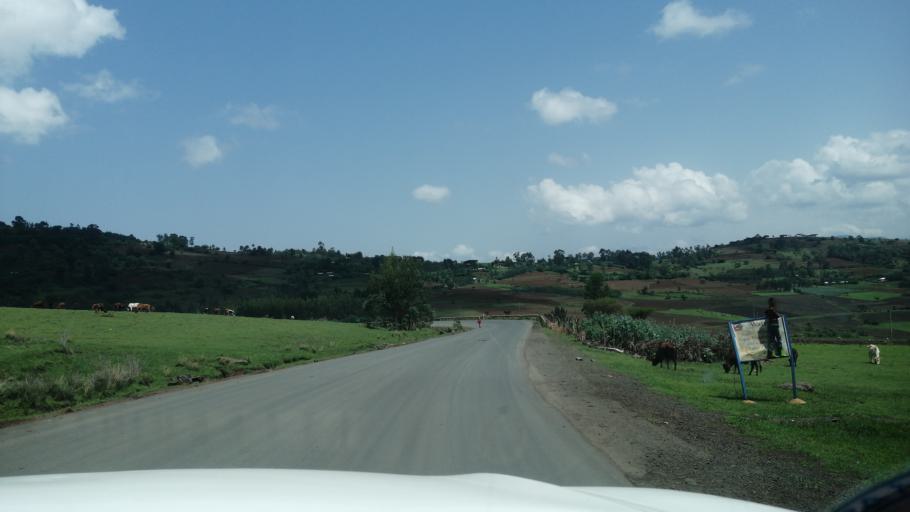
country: ET
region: Oromiya
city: Gedo
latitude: 8.9686
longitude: 37.5818
